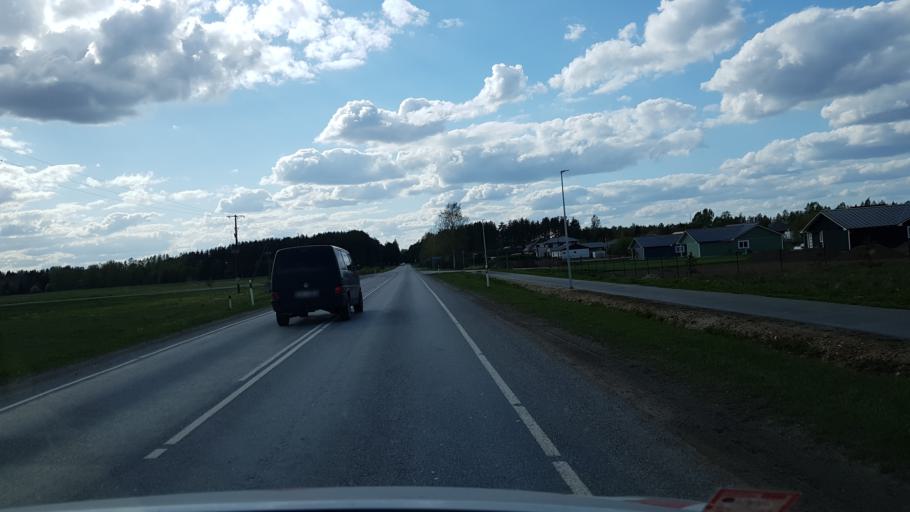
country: EE
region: Tartu
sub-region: UElenurme vald
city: Ulenurme
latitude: 58.3251
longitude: 26.7899
